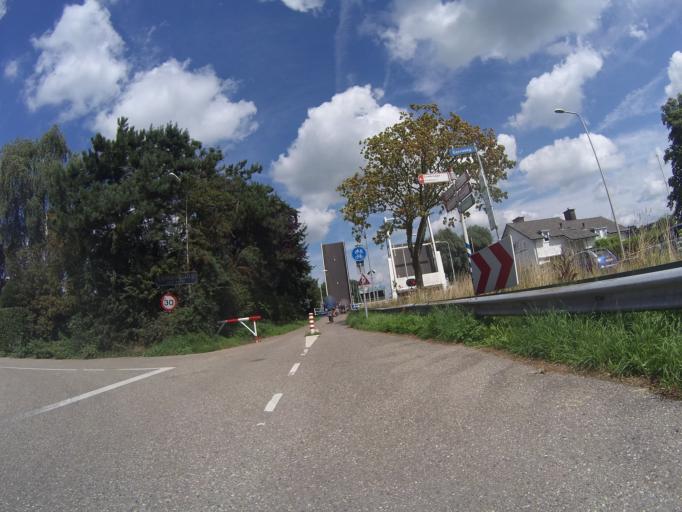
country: NL
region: Utrecht
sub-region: Gemeente Baarn
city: Baarn
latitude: 52.2252
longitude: 5.3126
